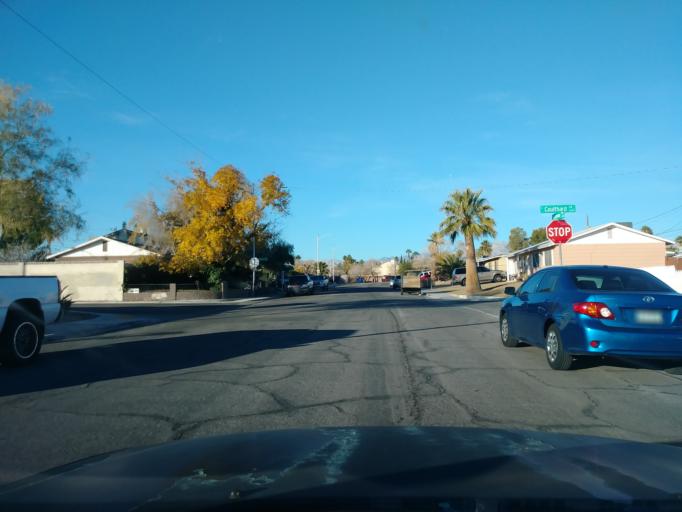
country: US
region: Nevada
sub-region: Clark County
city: Spring Valley
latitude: 36.1651
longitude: -115.2397
